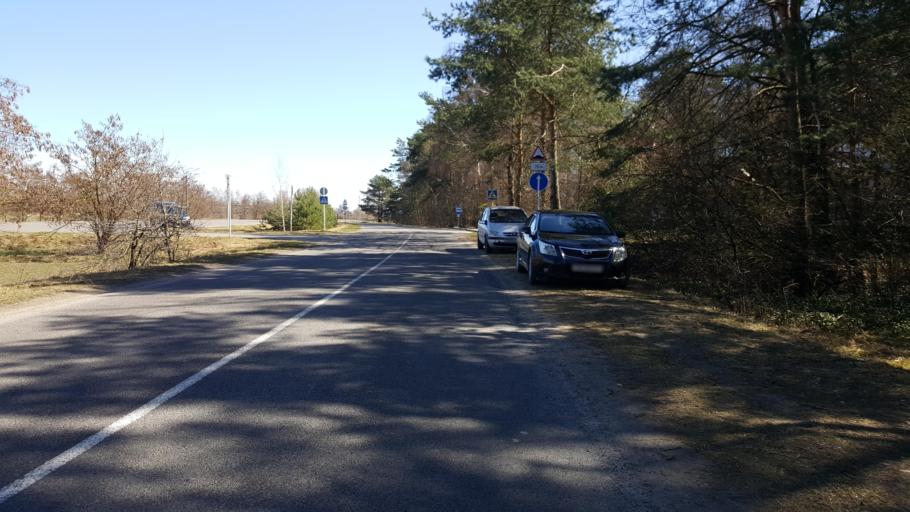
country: BY
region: Brest
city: Zhabinka
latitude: 52.2527
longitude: 23.8868
